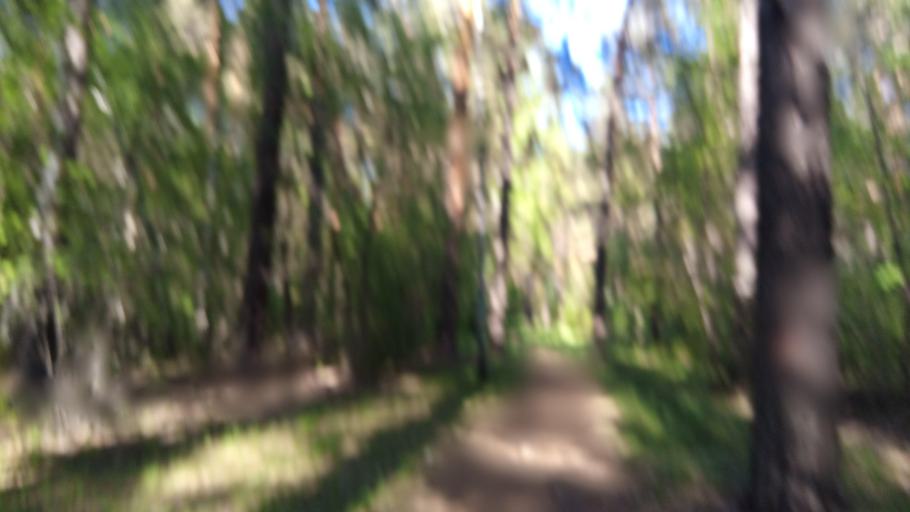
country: RU
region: Chelyabinsk
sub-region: Gorod Chelyabinsk
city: Chelyabinsk
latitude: 55.1476
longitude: 61.3466
